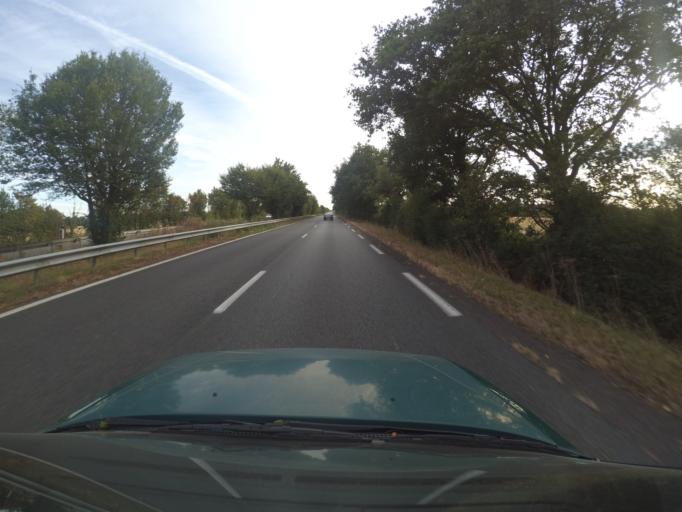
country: FR
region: Pays de la Loire
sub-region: Departement de la Vendee
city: Bouffere
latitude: 46.9349
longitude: -1.3587
